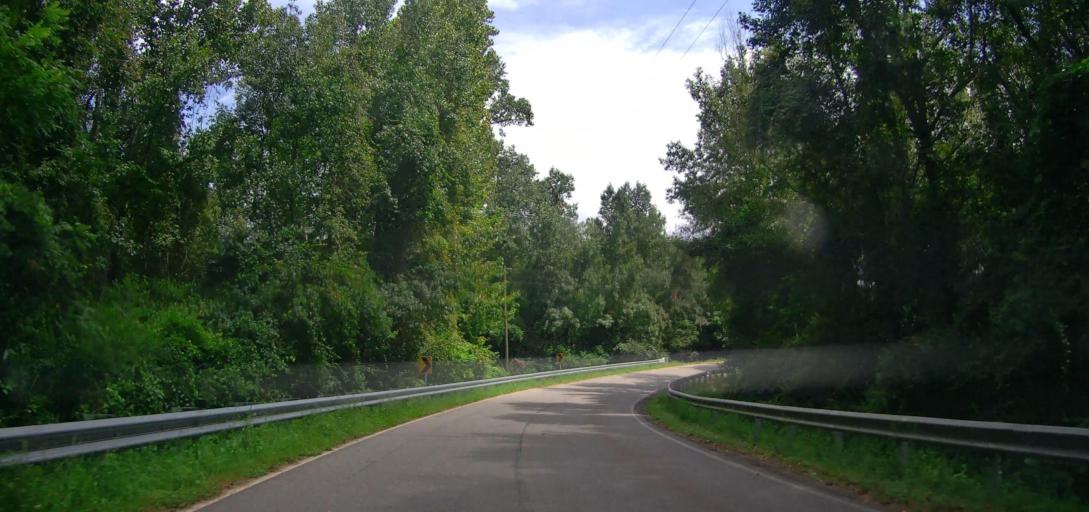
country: US
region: Georgia
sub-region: Houston County
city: Perry
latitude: 32.5223
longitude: -83.7474
